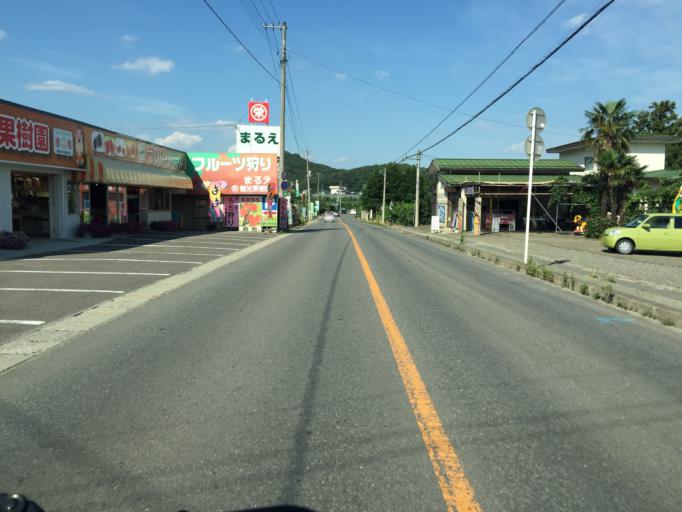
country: JP
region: Fukushima
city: Fukushima-shi
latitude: 37.8118
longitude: 140.4195
